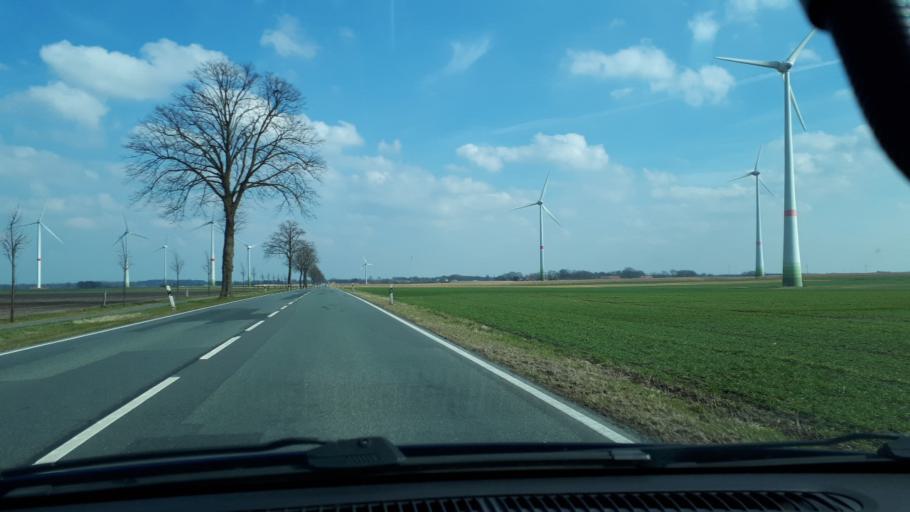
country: DE
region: Lower Saxony
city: Siedenburg
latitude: 52.6734
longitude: 8.9296
